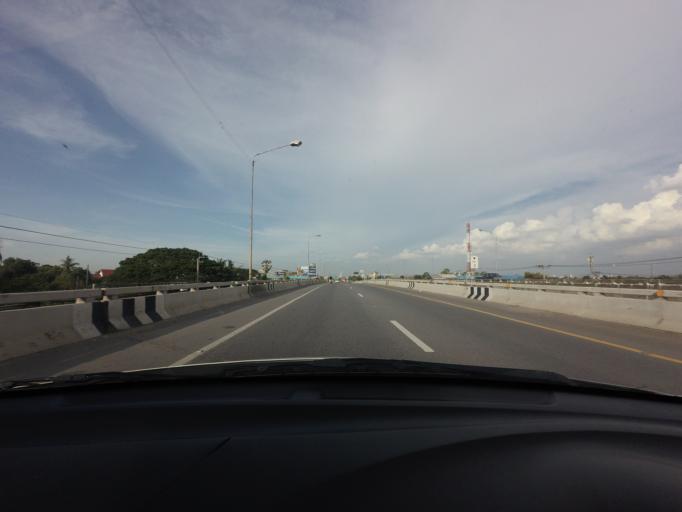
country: TH
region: Nonthaburi
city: Bang Bua Thong
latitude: 13.9483
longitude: 100.4443
